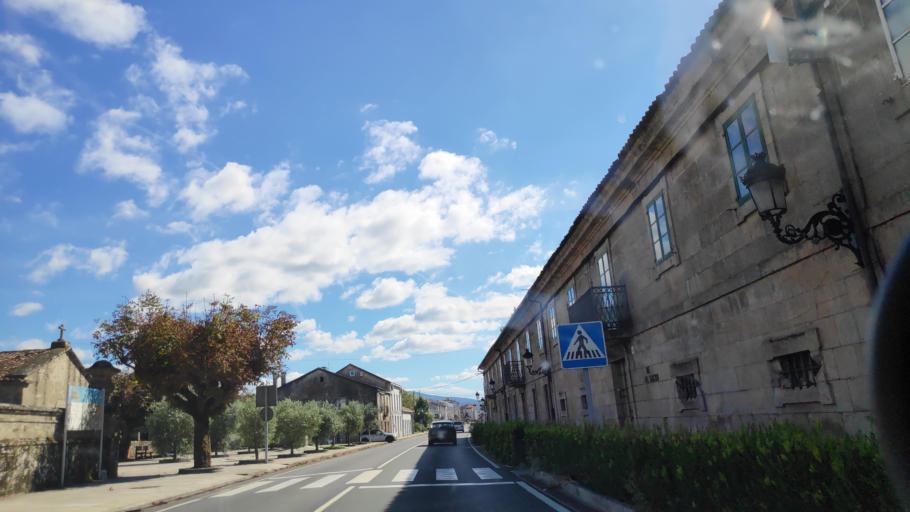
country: ES
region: Galicia
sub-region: Provincia da Coruna
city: Padron
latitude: 42.7461
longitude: -8.6556
